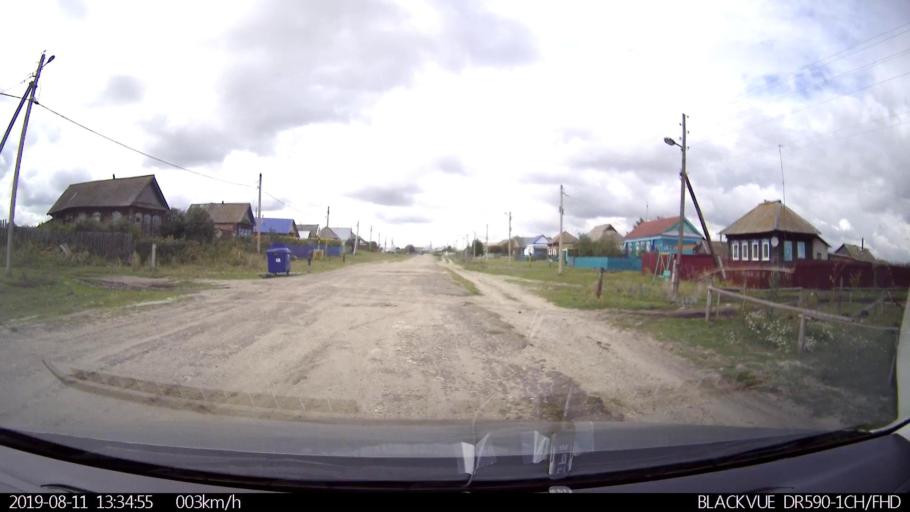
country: RU
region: Ulyanovsk
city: Ignatovka
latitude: 53.8597
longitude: 47.5917
